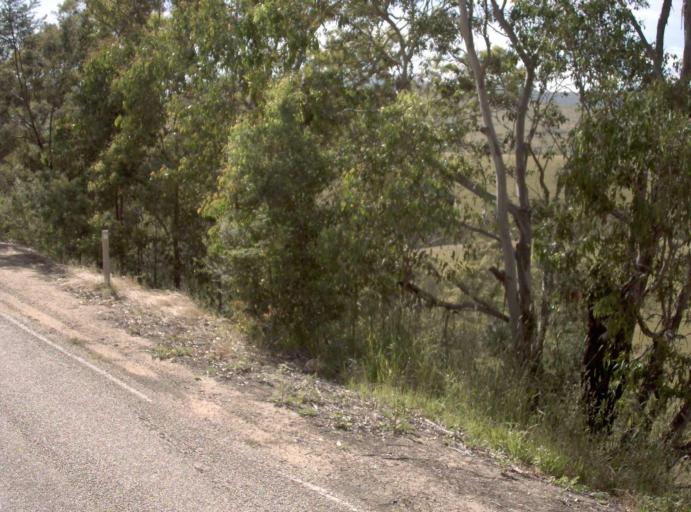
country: AU
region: Victoria
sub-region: East Gippsland
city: Lakes Entrance
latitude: -37.5109
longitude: 148.1688
